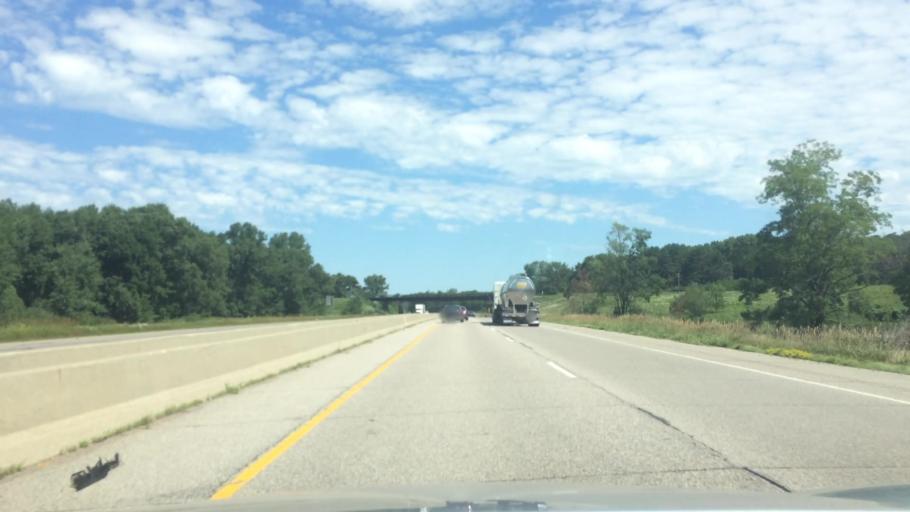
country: US
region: Wisconsin
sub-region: Marquette County
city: Westfield
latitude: 43.7475
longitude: -89.4824
